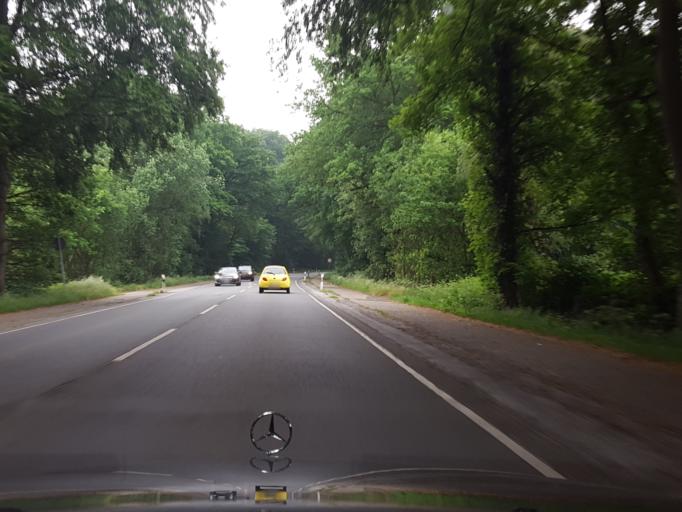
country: DE
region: North Rhine-Westphalia
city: Oer-Erkenschwick
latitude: 51.6821
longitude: 7.2958
